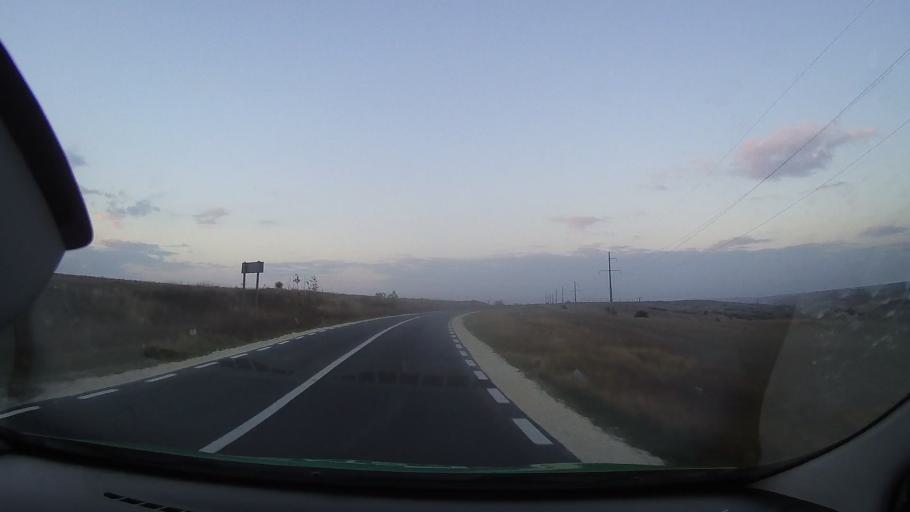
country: RO
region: Constanta
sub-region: Comuna Baneasa
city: Baneasa
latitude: 44.0811
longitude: 27.6892
